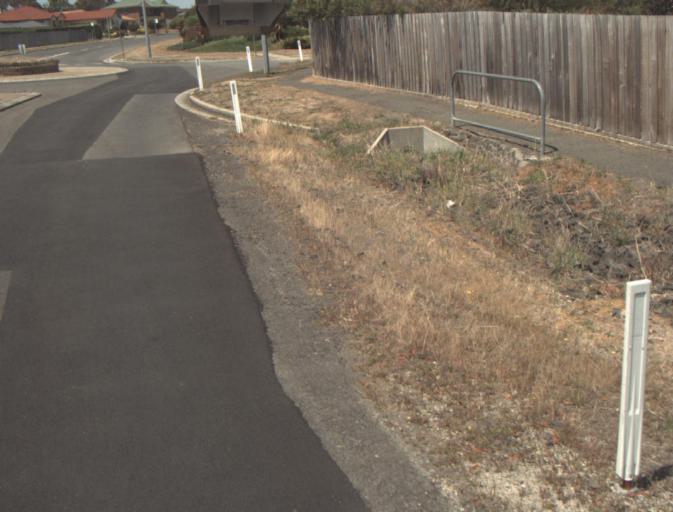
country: AU
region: Tasmania
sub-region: Launceston
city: Newstead
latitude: -41.4773
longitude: 147.1822
